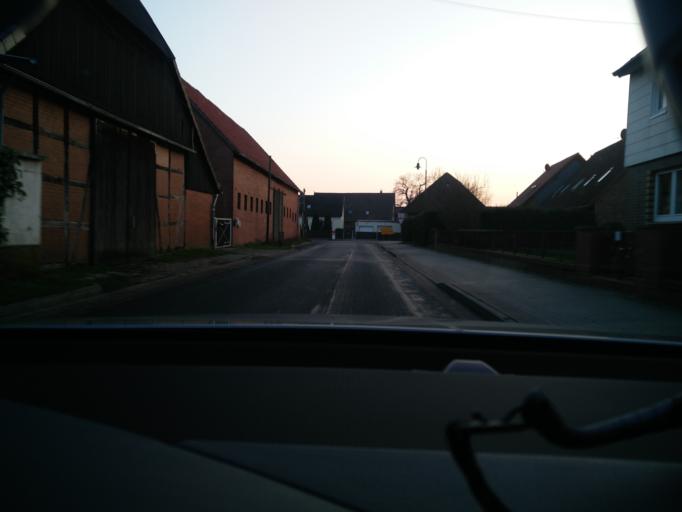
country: DE
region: Lower Saxony
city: Sehnde
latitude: 52.3175
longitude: 10.0252
